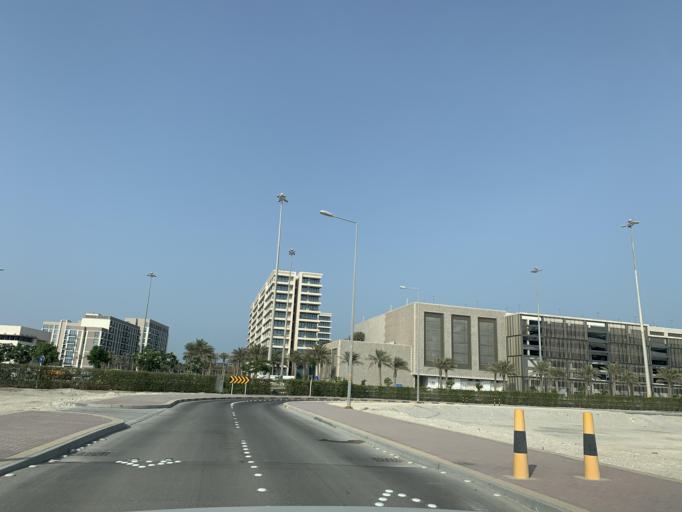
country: BH
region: Muharraq
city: Al Muharraq
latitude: 26.3041
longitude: 50.6393
